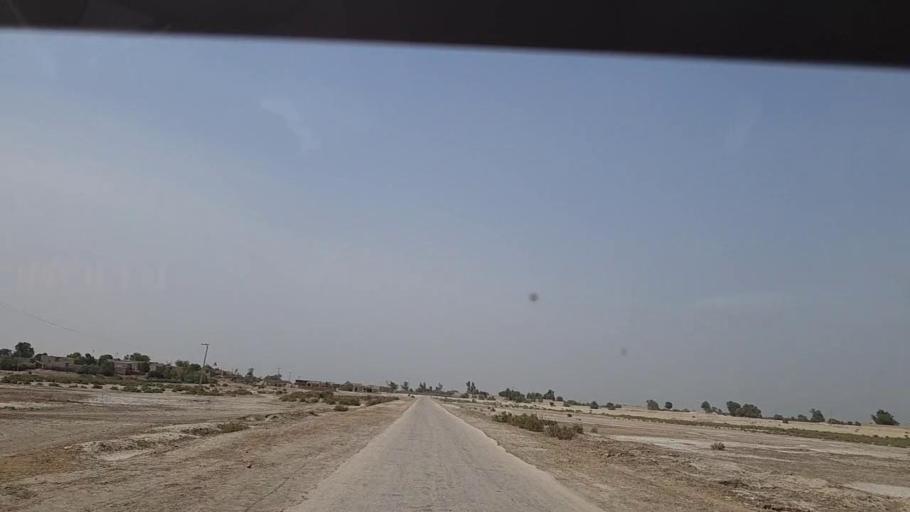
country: PK
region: Sindh
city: Khairpur Nathan Shah
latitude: 27.0701
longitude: 67.6512
